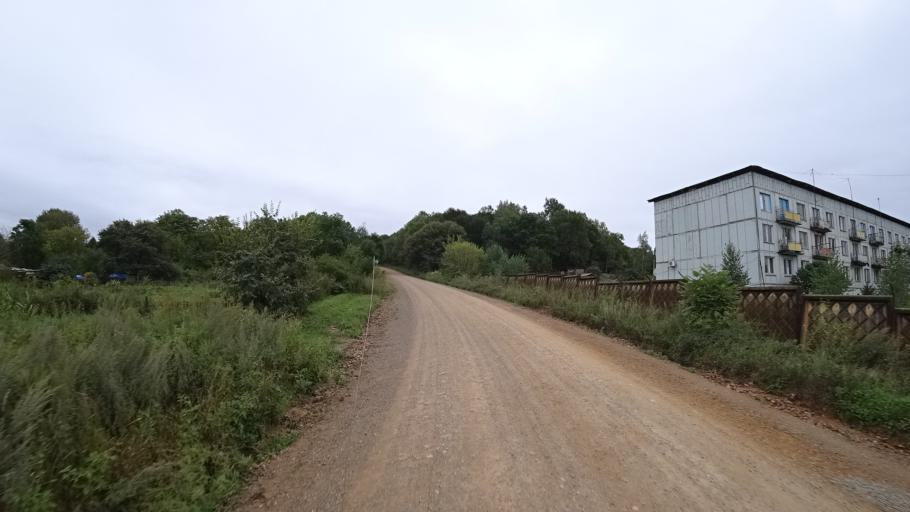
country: RU
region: Primorskiy
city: Rettikhovka
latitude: 44.1721
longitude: 132.8795
